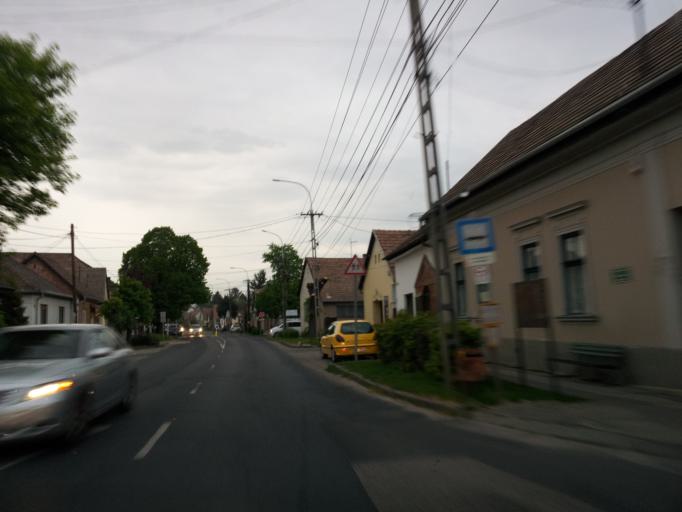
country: HU
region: Pest
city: Dunabogdany
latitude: 47.7937
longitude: 19.0362
